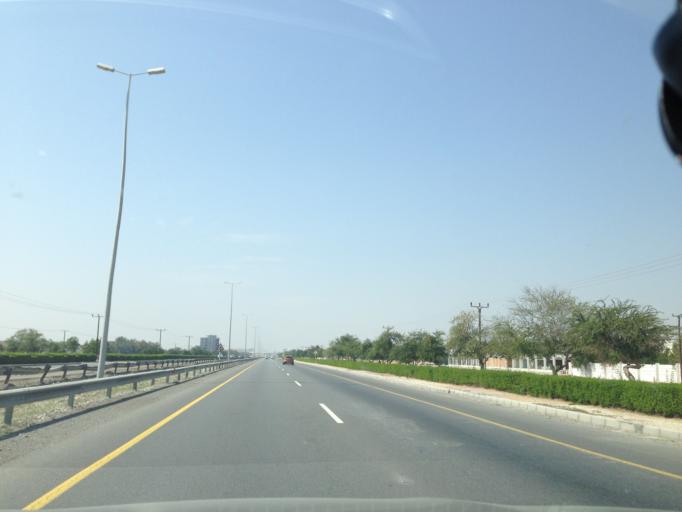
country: OM
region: Al Batinah
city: Barka'
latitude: 23.6607
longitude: 57.9164
